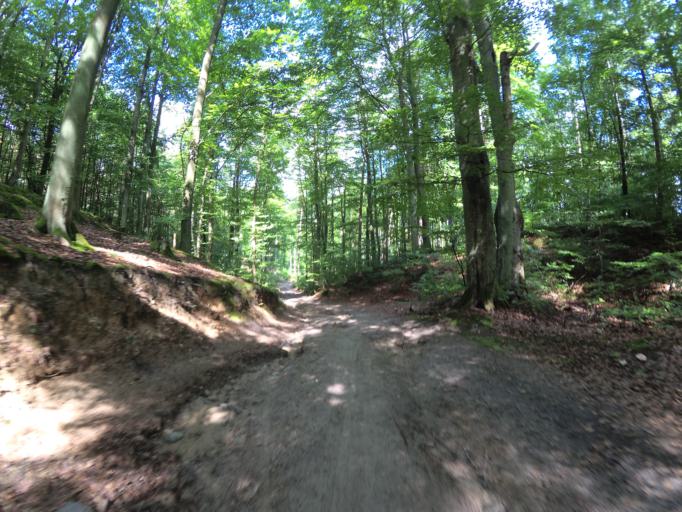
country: PL
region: Pomeranian Voivodeship
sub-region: Gdynia
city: Wielki Kack
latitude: 54.5073
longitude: 18.4571
